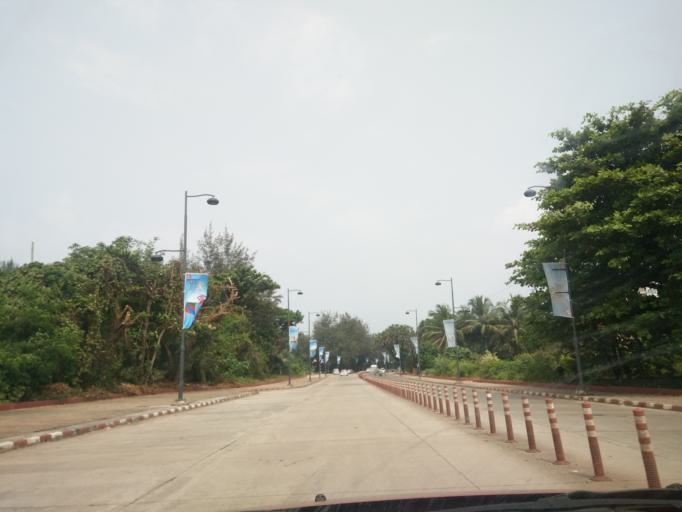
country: IN
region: Goa
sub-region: North Goa
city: Taleigao
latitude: 15.4746
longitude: 73.8085
